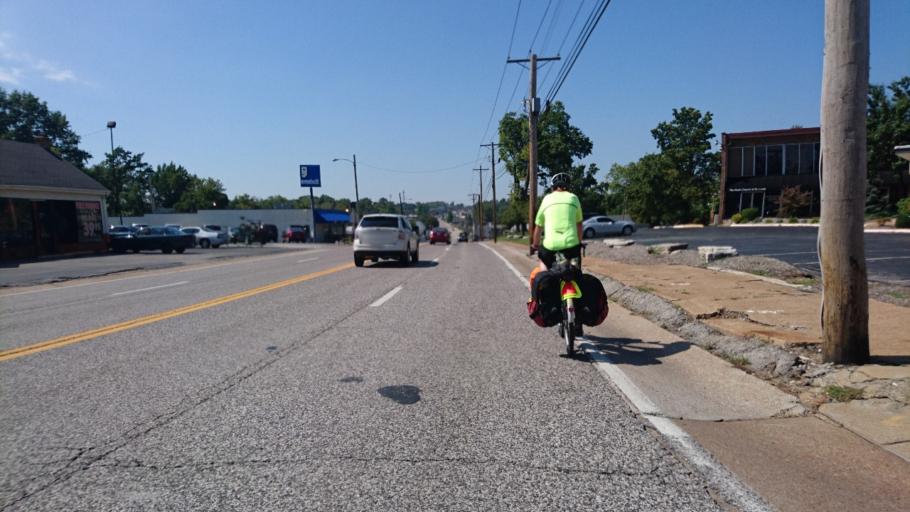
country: US
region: Missouri
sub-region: Saint Louis County
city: Brentwood
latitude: 38.6125
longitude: -90.3549
